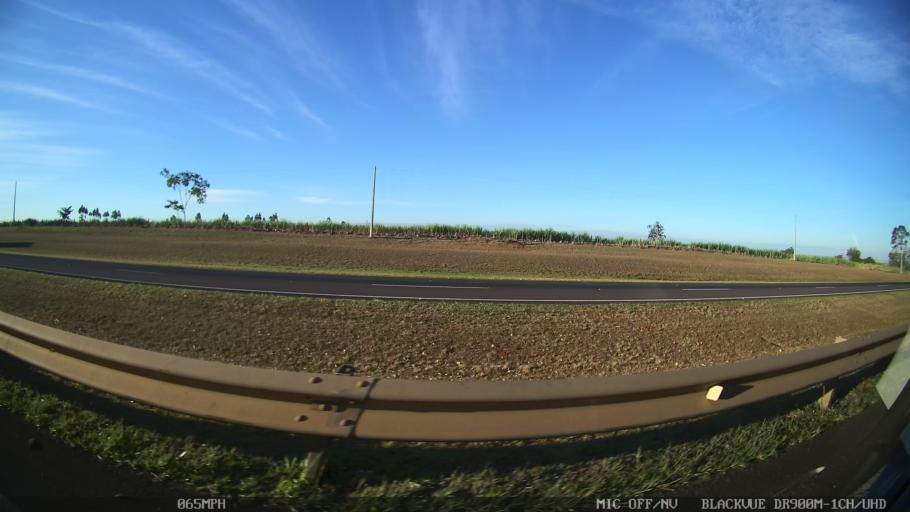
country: BR
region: Sao Paulo
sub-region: Guapiacu
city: Guapiacu
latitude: -20.9969
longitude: -49.1983
